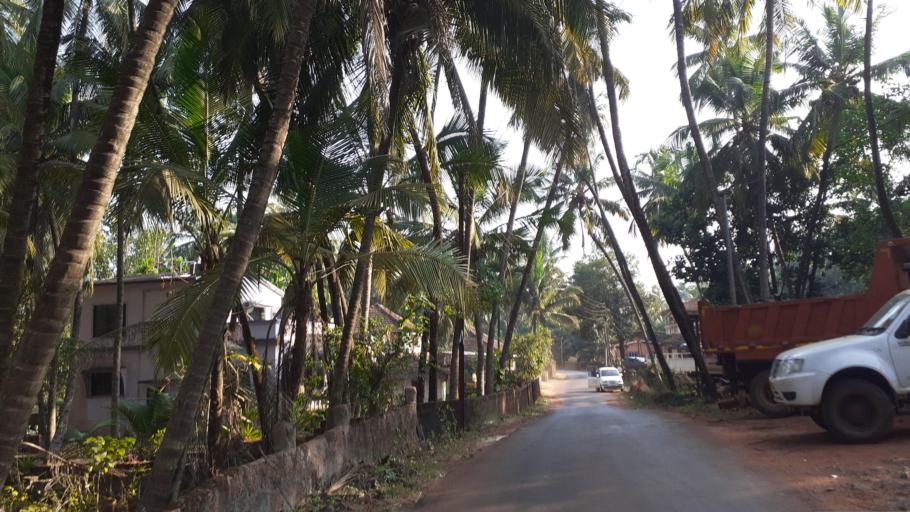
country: IN
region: Maharashtra
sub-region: Ratnagiri
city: Ratnagiri
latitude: 17.2168
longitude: 73.2476
